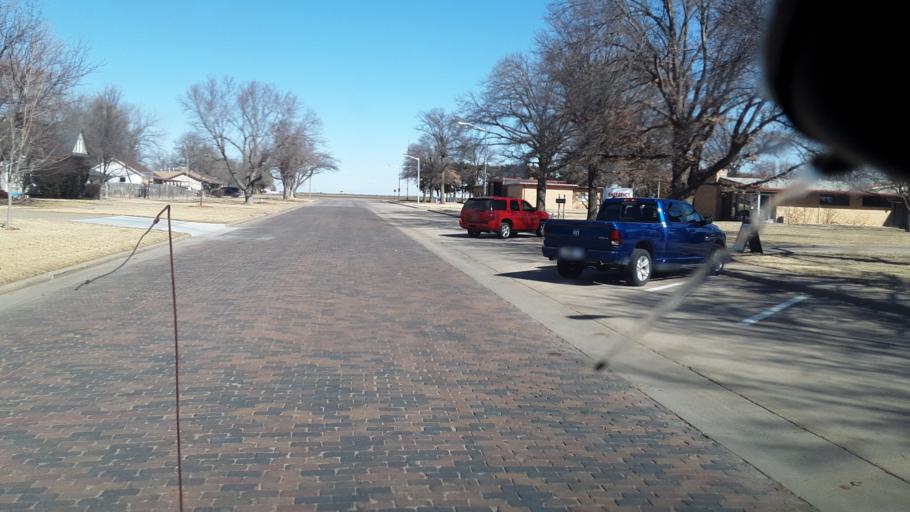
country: US
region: Kansas
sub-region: Barton County
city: Ellinwood
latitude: 38.3604
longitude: -98.5812
